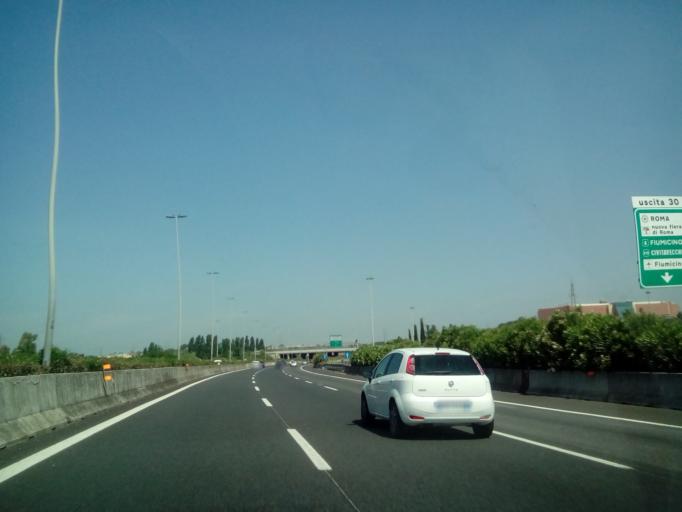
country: IT
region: Latium
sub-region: Citta metropolitana di Roma Capitale
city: Vitinia
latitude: 41.8146
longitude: 12.3941
